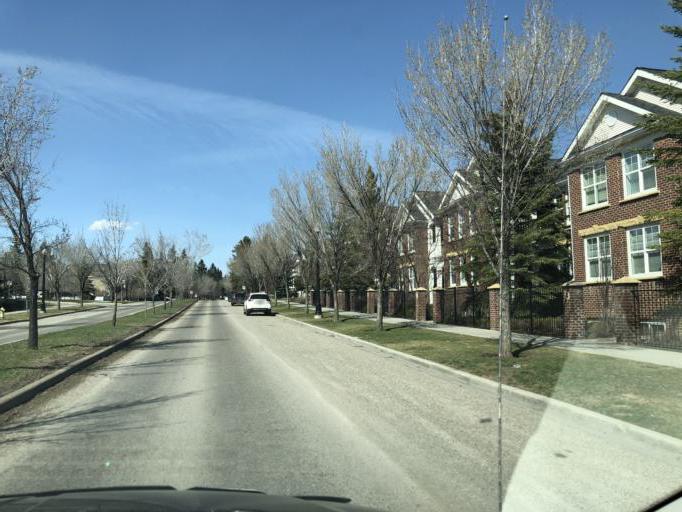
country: CA
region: Alberta
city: Calgary
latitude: 51.0172
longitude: -114.1137
